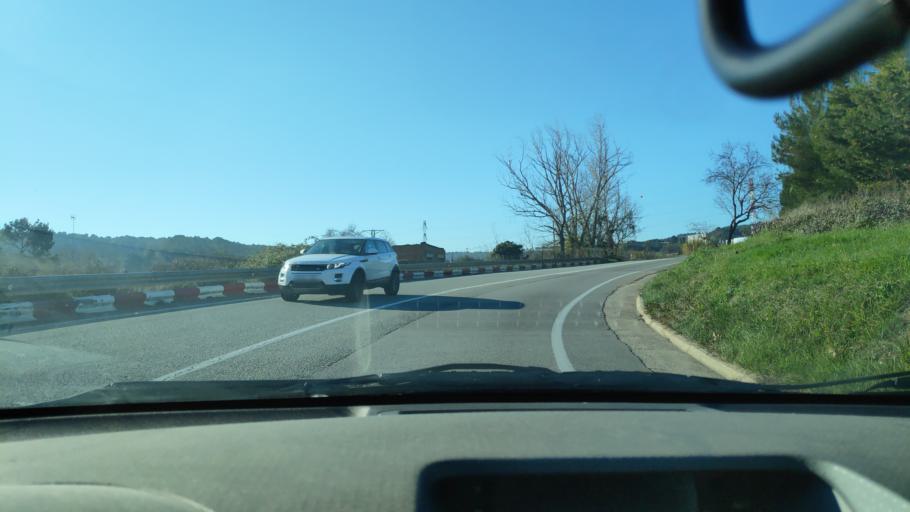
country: ES
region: Catalonia
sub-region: Provincia de Barcelona
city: Sant Quirze del Valles
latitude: 41.5240
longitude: 2.0853
